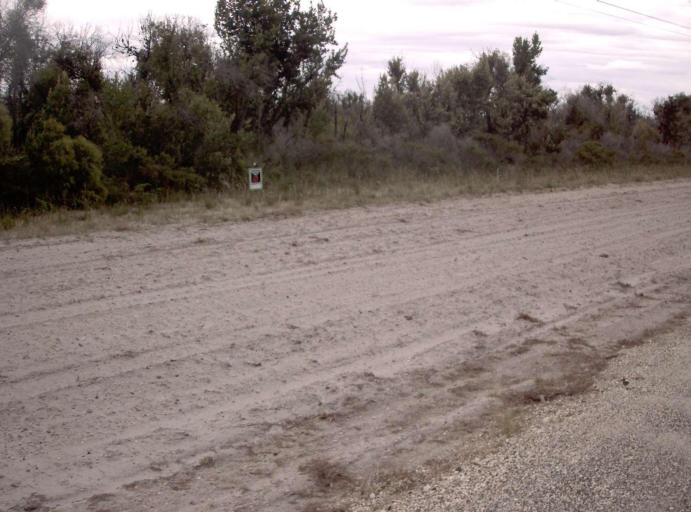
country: AU
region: Victoria
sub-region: East Gippsland
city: Bairnsdale
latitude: -38.1011
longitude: 147.5035
